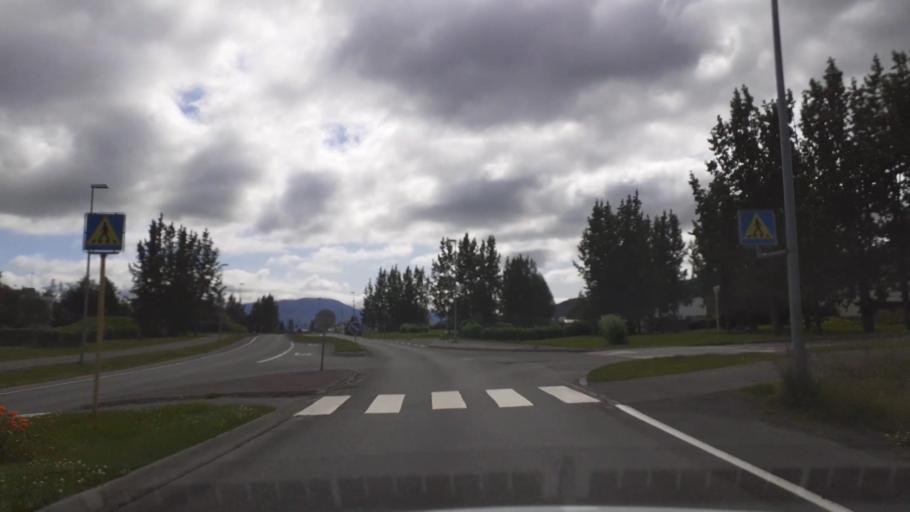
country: IS
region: Northeast
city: Akureyri
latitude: 65.6802
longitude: -18.1163
